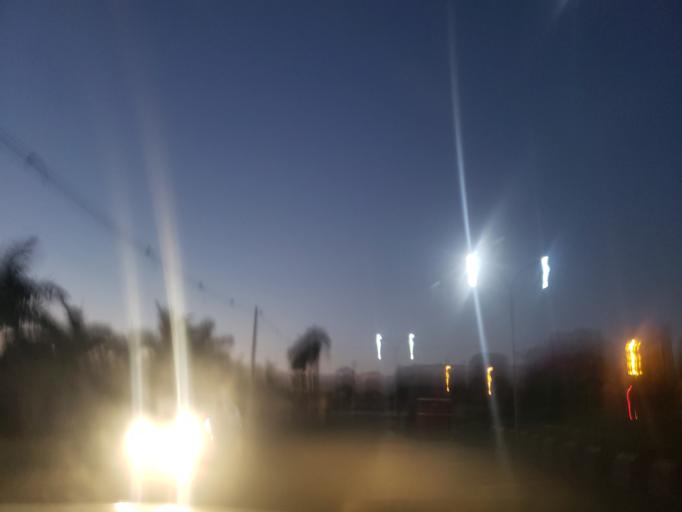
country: BR
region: Sao Paulo
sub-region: Conchal
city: Conchal
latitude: -22.2901
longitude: -47.1344
